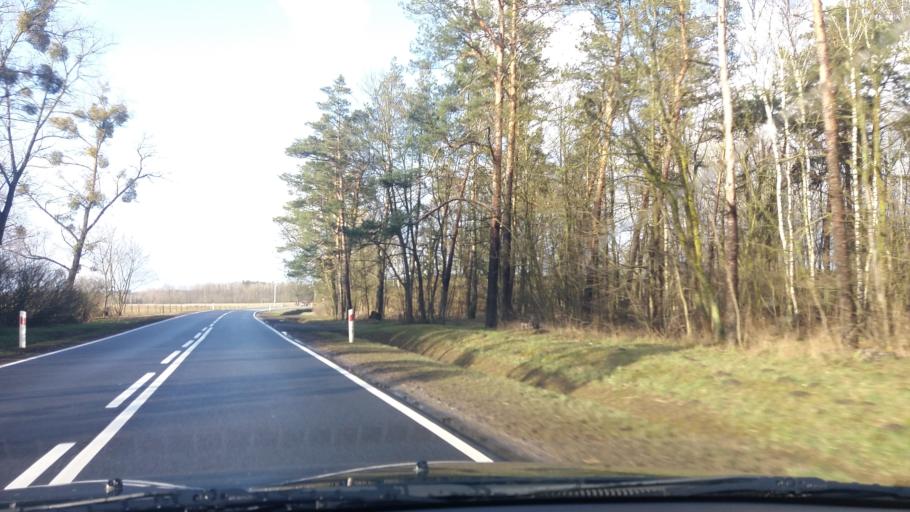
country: PL
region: Masovian Voivodeship
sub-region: Powiat przasnyski
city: Chorzele
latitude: 53.3201
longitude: 20.9067
